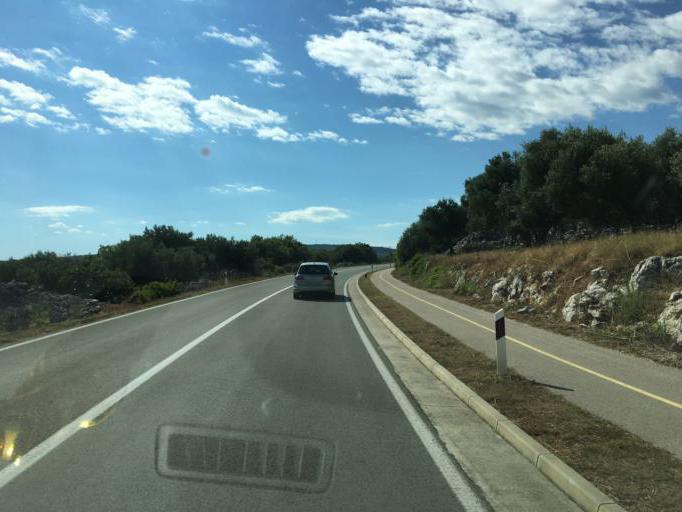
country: HR
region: Primorsko-Goranska
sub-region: Grad Krk
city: Krk
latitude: 45.0340
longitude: 14.5779
